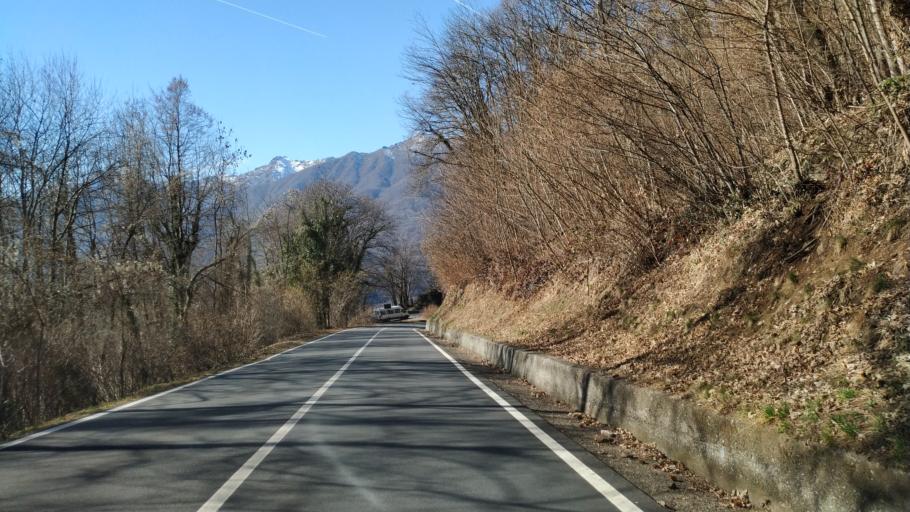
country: IT
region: Piedmont
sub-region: Provincia di Vercelli
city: Civiasco
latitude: 45.8038
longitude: 8.2881
